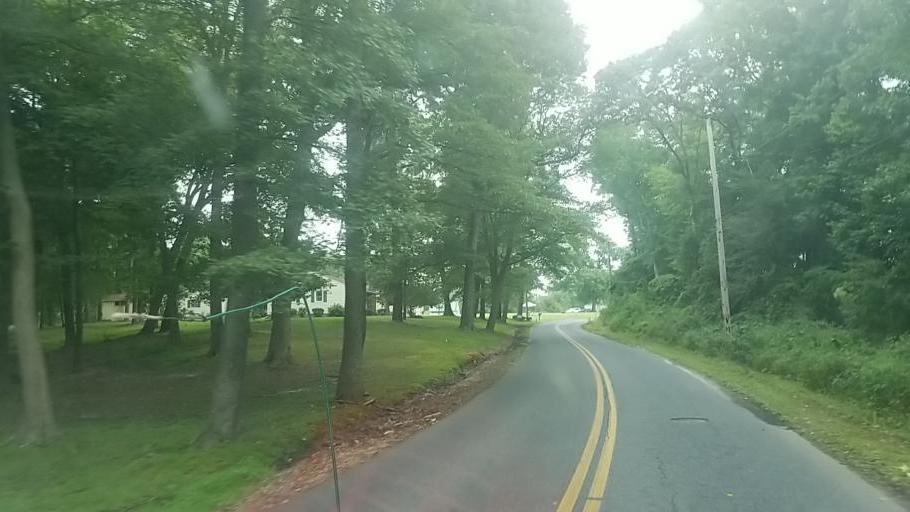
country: US
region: Delaware
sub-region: Sussex County
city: Selbyville
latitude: 38.4344
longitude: -75.1943
